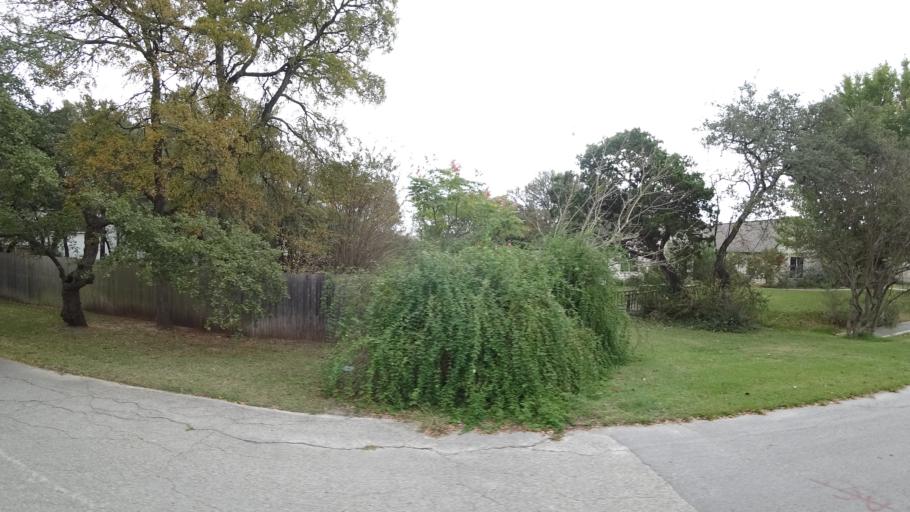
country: US
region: Texas
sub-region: Travis County
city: Barton Creek
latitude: 30.2562
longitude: -97.9085
